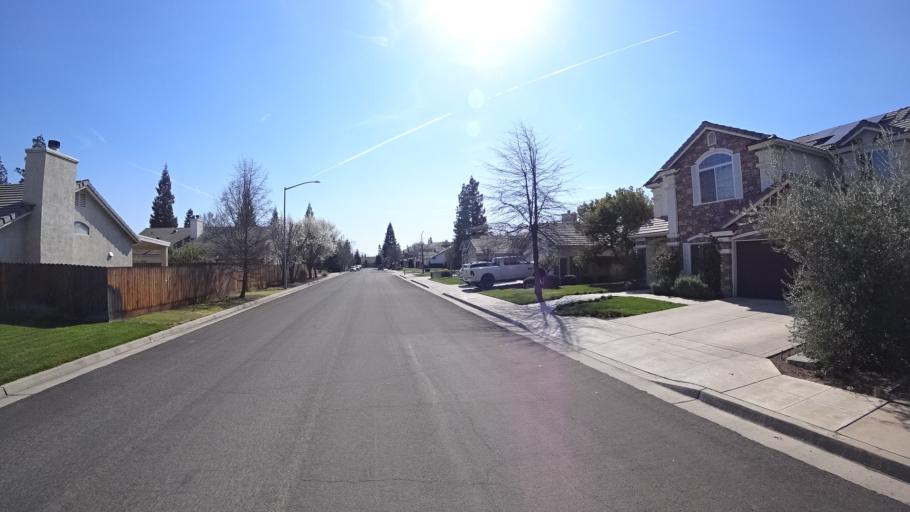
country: US
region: California
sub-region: Fresno County
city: Clovis
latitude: 36.8864
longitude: -119.7468
